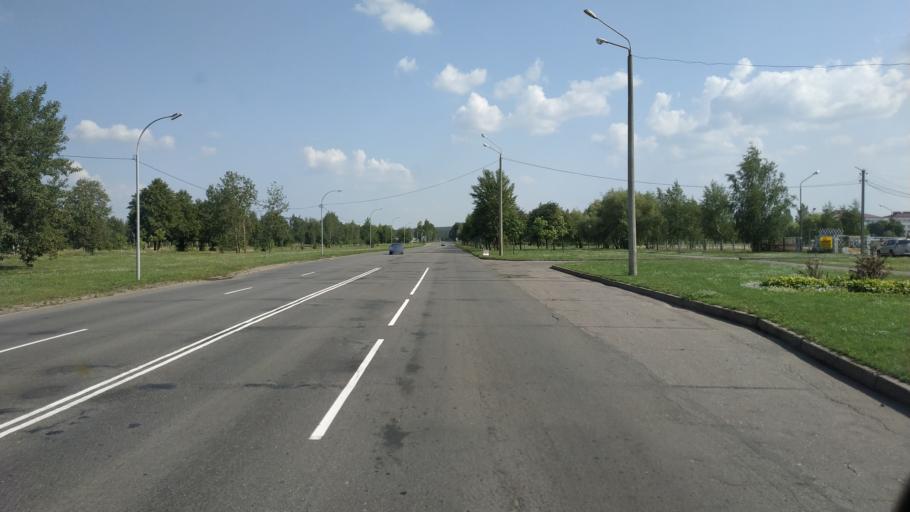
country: BY
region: Mogilev
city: Buynichy
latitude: 53.8603
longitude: 30.3245
